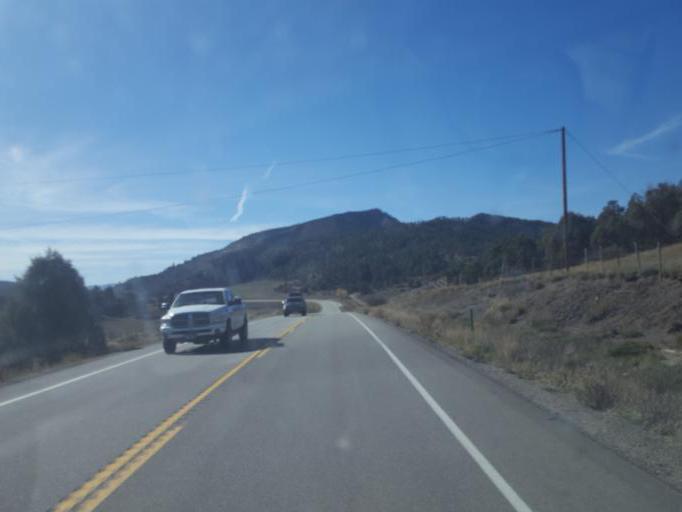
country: US
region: Colorado
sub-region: Archuleta County
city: Pagosa Springs
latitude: 37.2290
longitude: -107.2053
